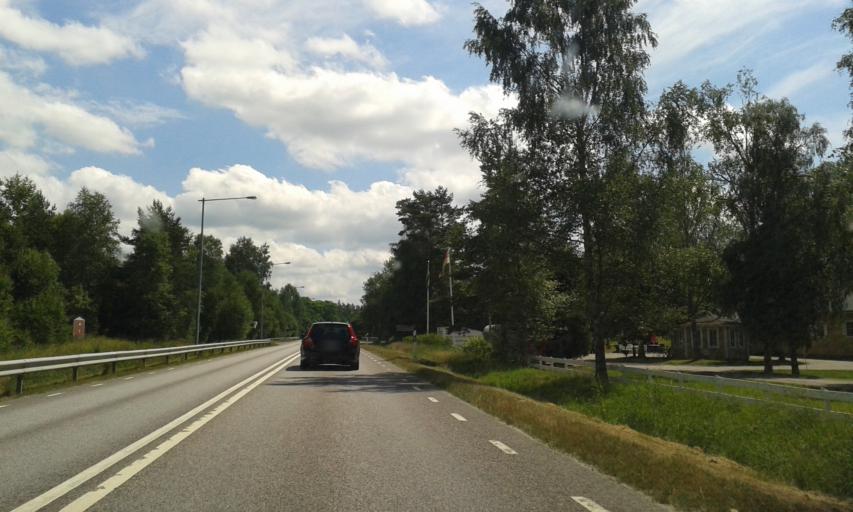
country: SE
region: Joenkoeping
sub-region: Varnamo Kommun
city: Rydaholm
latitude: 56.9716
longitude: 14.3264
